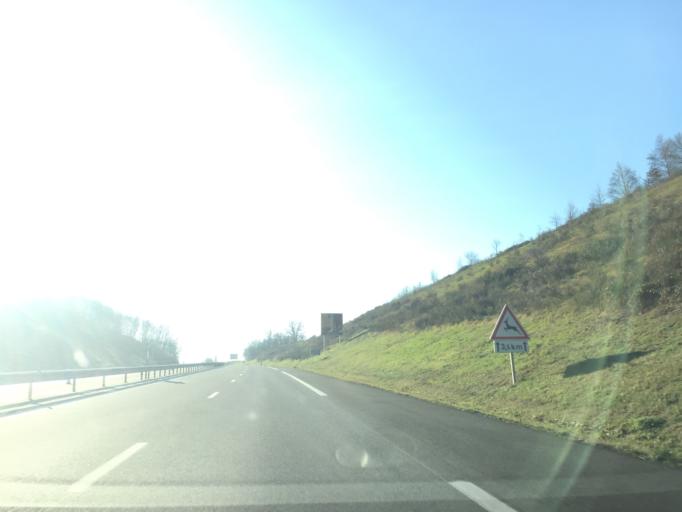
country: FR
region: Limousin
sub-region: Departement de la Correze
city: Varetz
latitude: 45.1867
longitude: 1.4811
